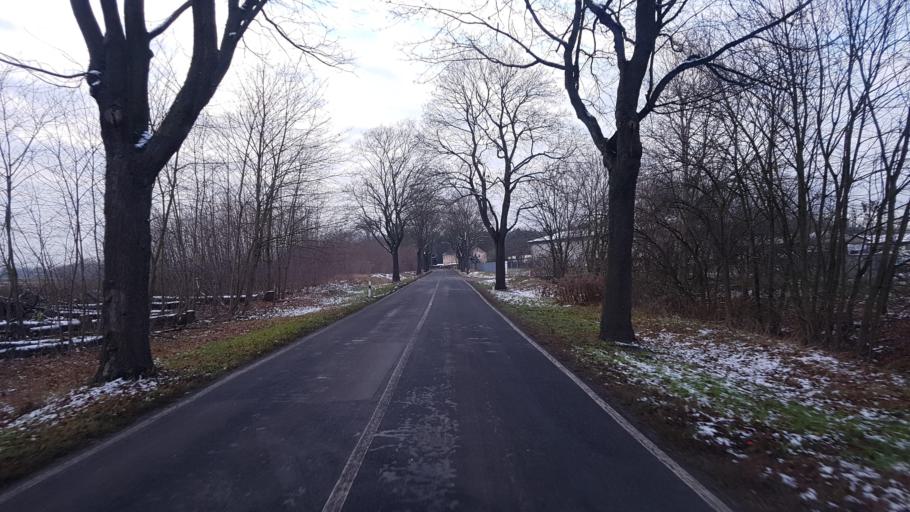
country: DE
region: Brandenburg
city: Rehfelde
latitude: 52.5099
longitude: 13.8800
